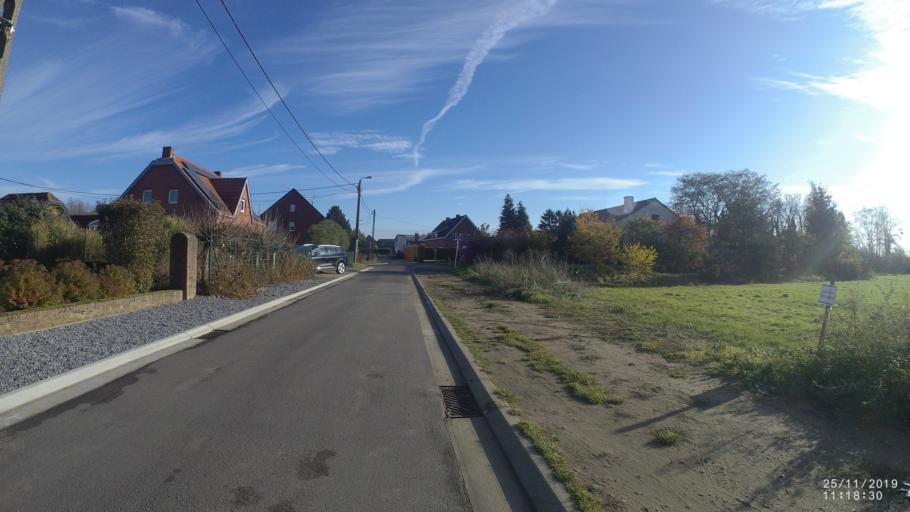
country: BE
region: Flanders
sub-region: Provincie Vlaams-Brabant
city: Aarschot
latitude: 51.0037
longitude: 4.8337
